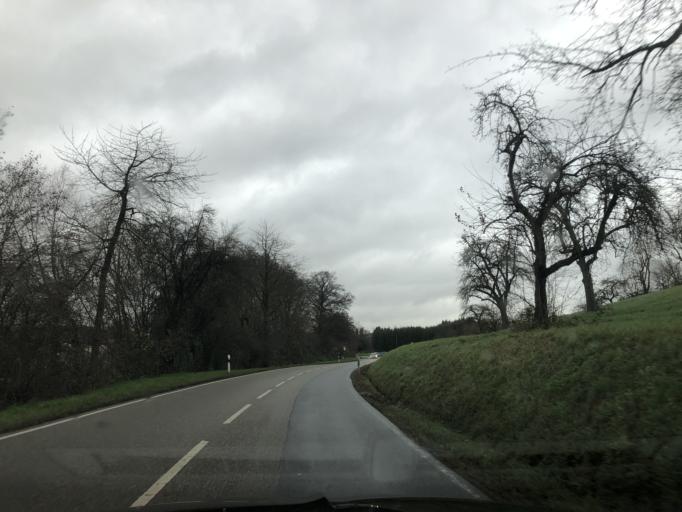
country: DE
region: Baden-Wuerttemberg
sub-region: Karlsruhe Region
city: Bammental
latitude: 49.3309
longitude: 8.7580
